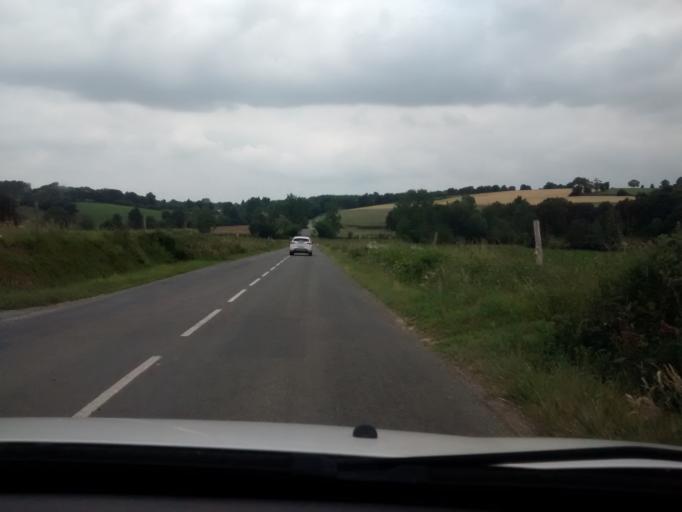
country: FR
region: Brittany
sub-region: Departement d'Ille-et-Vilaine
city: La Bouexiere
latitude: 48.1938
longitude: -1.4649
